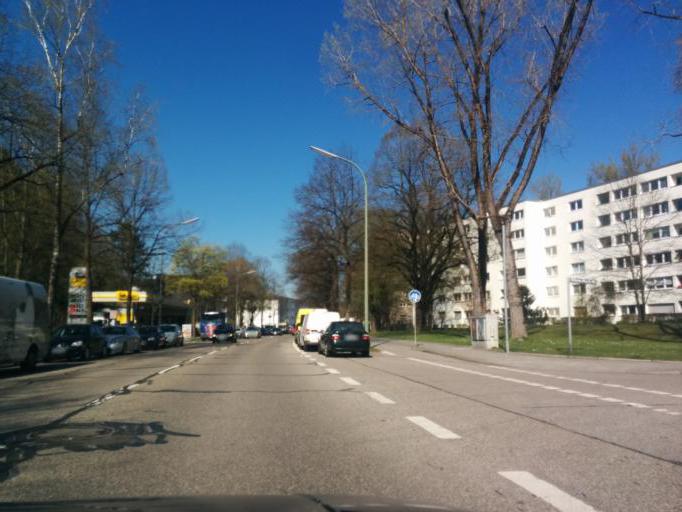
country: DE
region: Bavaria
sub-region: Upper Bavaria
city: Pullach im Isartal
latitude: 48.0787
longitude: 11.5057
